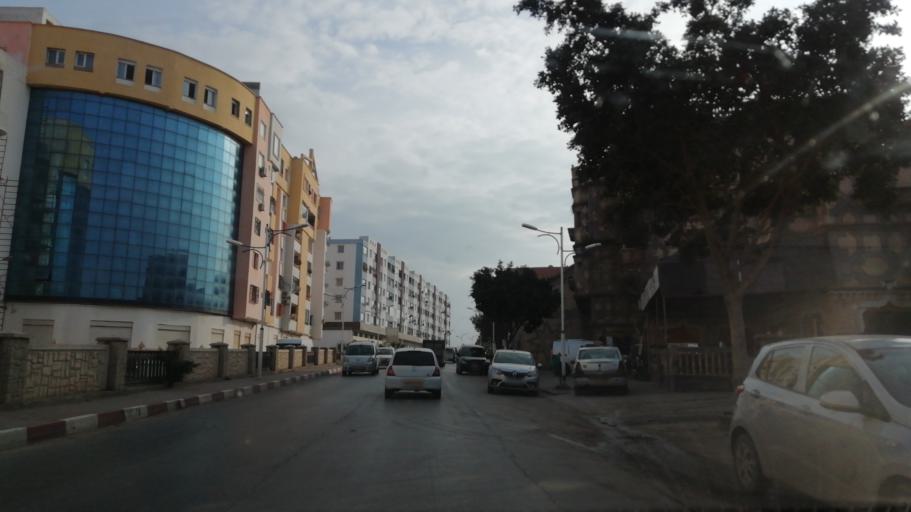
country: DZ
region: Mostaganem
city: Mostaganem
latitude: 35.8937
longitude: 0.0760
